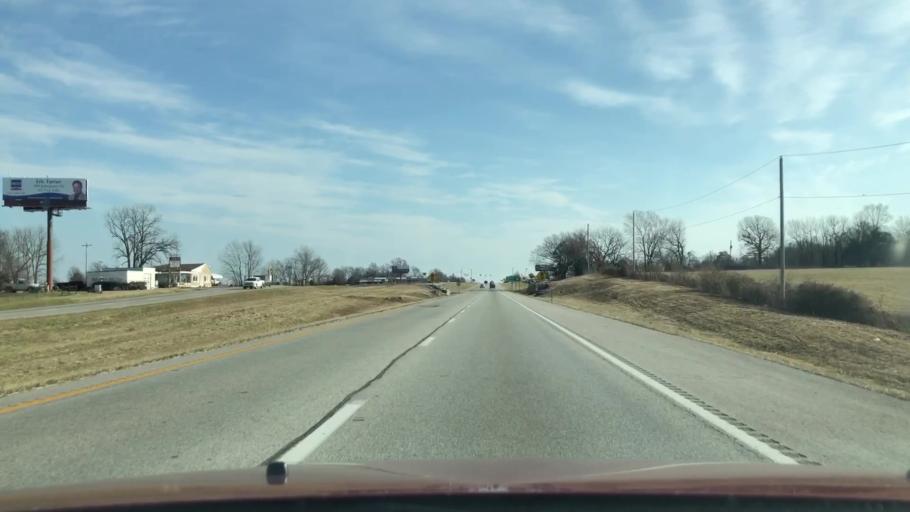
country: US
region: Missouri
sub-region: Webster County
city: Rogersville
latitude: 37.1188
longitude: -93.1265
